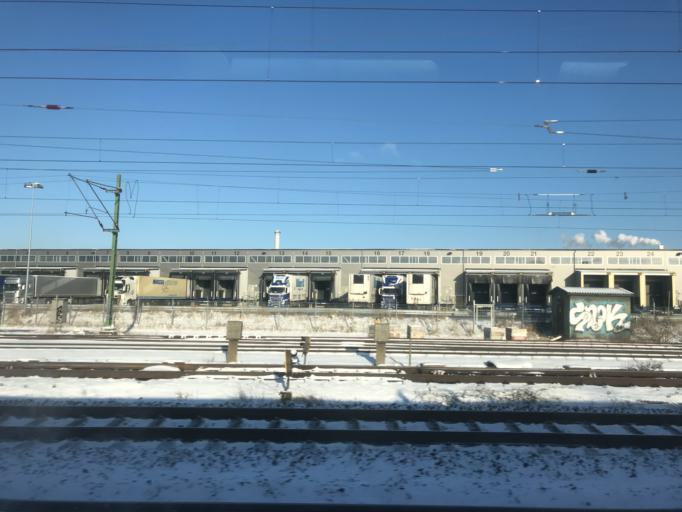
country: SE
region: Skane
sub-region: Burlovs Kommun
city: Arloev
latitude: 55.6223
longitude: 13.0522
